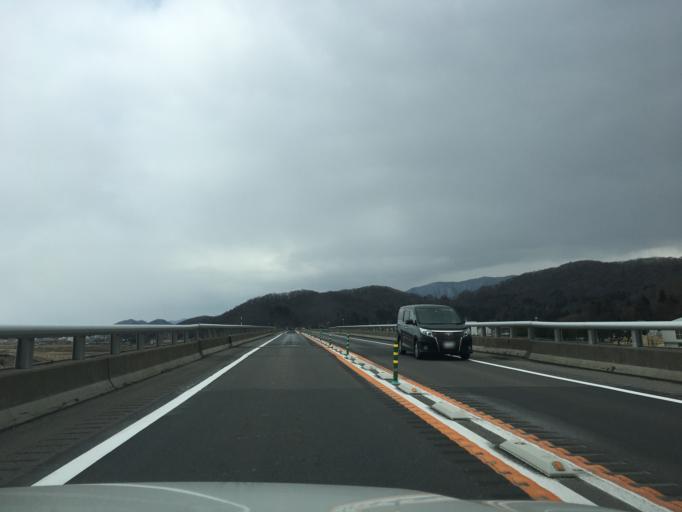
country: JP
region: Aomori
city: Aomori Shi
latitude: 40.8089
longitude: 140.8005
